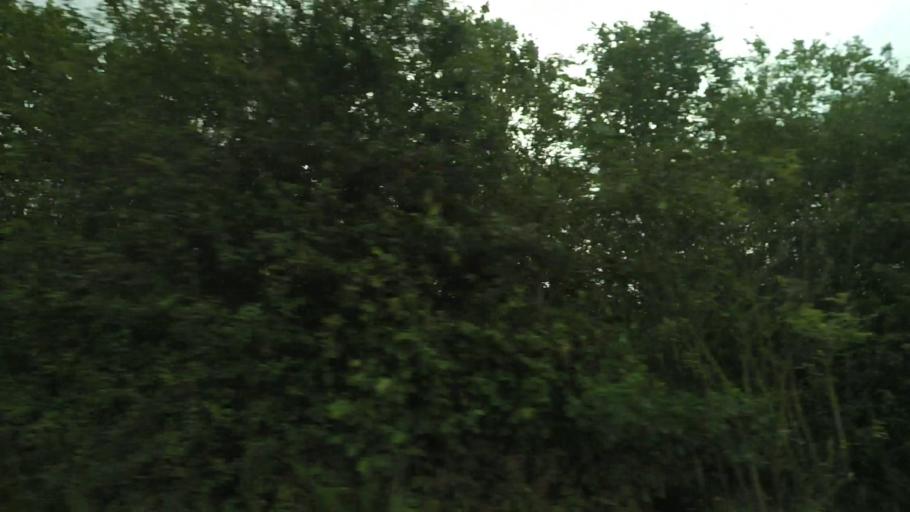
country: DK
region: Central Jutland
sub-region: Syddjurs Kommune
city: Ryomgard
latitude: 56.4383
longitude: 10.5605
